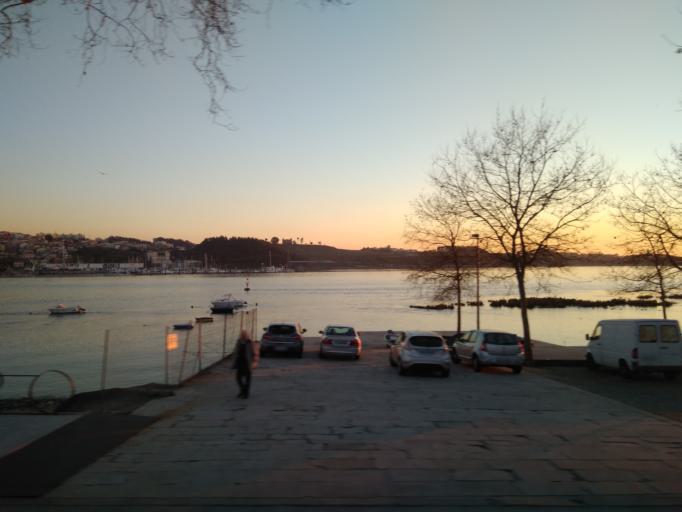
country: PT
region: Porto
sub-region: Vila Nova de Gaia
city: Canidelo
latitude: 41.1482
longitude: -8.6519
